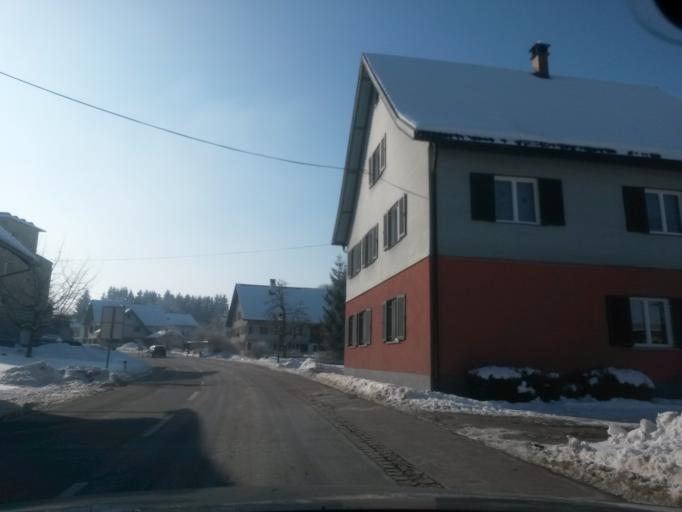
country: AT
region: Vorarlberg
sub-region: Politischer Bezirk Bregenz
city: Hohenweiler
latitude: 47.5793
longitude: 9.7759
